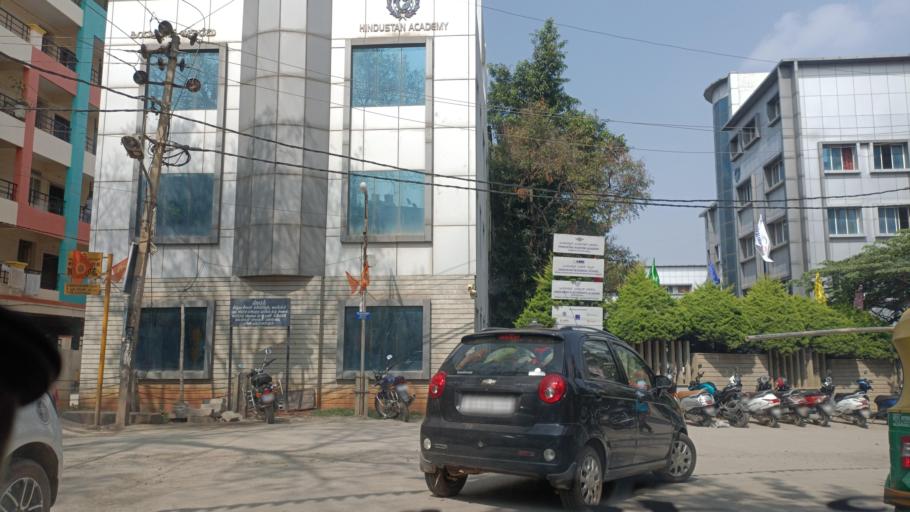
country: IN
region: Karnataka
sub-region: Bangalore Urban
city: Bangalore
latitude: 12.9597
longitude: 77.7029
